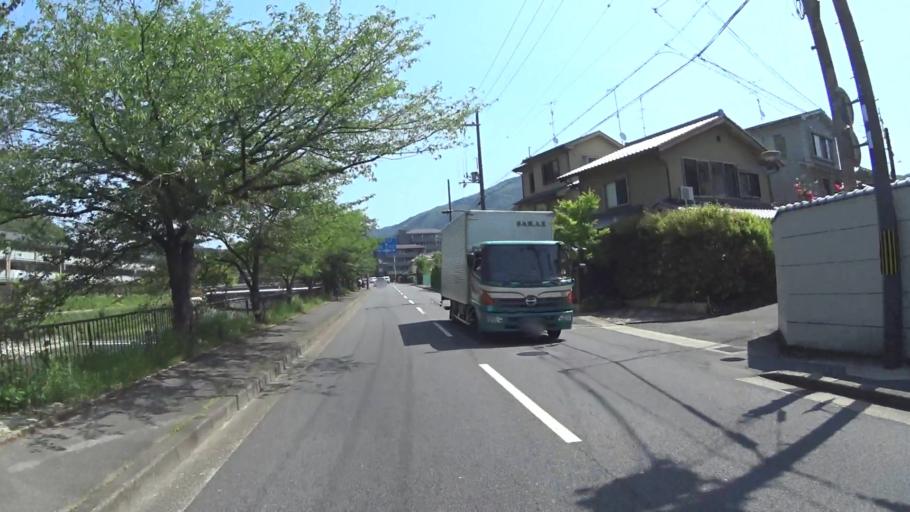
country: JP
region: Kyoto
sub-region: Kyoto-shi
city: Kamigyo-ku
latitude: 35.0500
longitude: 135.7877
